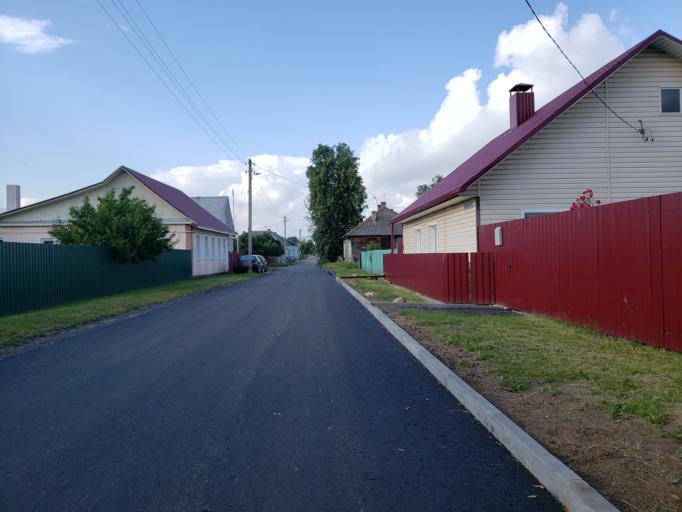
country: BY
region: Minsk
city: Chervyen'
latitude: 53.7082
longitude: 28.4270
